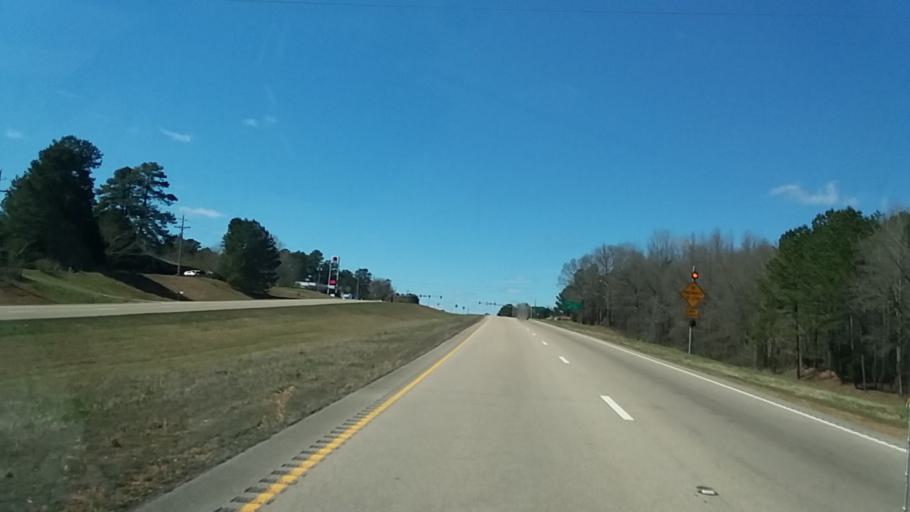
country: US
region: Mississippi
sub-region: Alcorn County
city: Farmington
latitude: 34.8769
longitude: -88.4378
